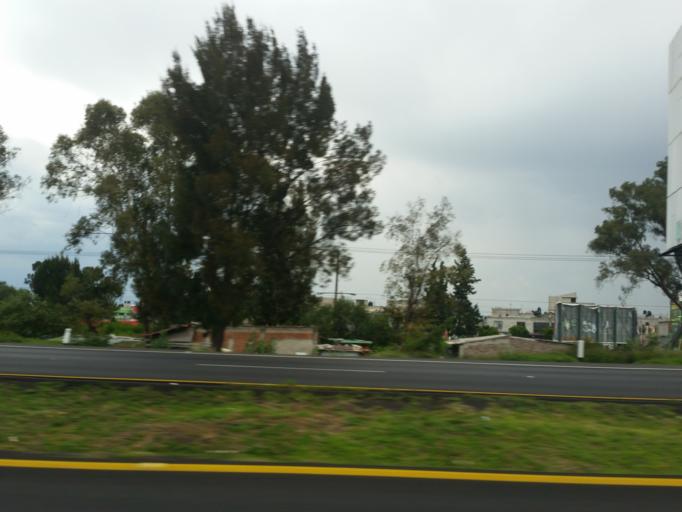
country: MX
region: Mexico
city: Santo Tomas Chiconautla
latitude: 19.6175
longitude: -99.0125
